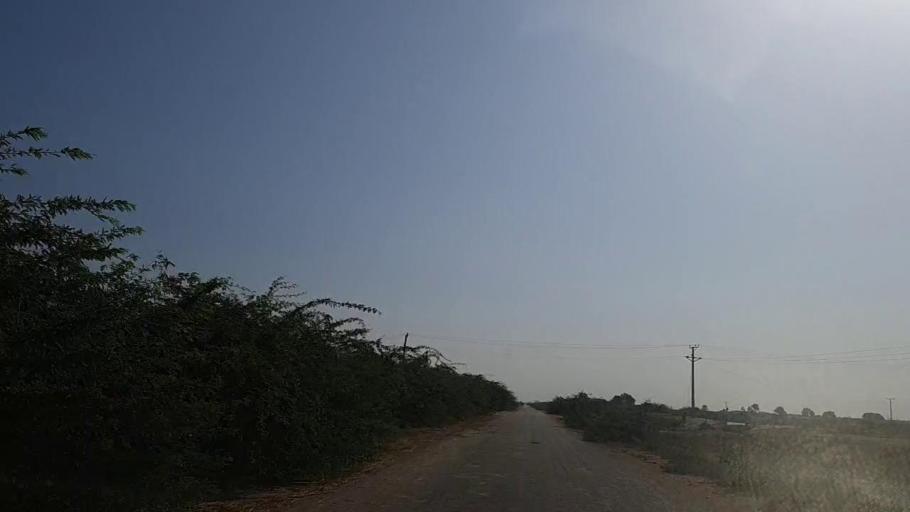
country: PK
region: Sindh
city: Jati
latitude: 24.4555
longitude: 68.2646
